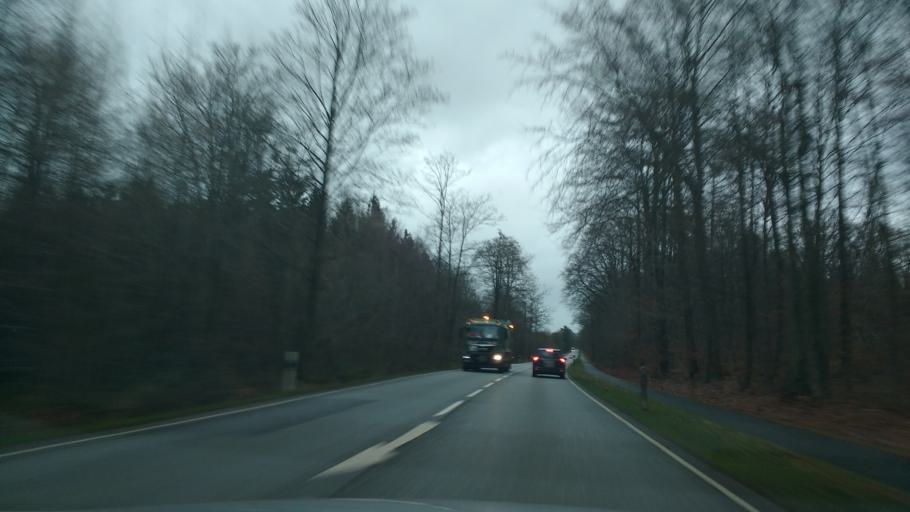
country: DE
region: Schleswig-Holstein
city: Oelixdorf
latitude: 53.9463
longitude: 9.5454
